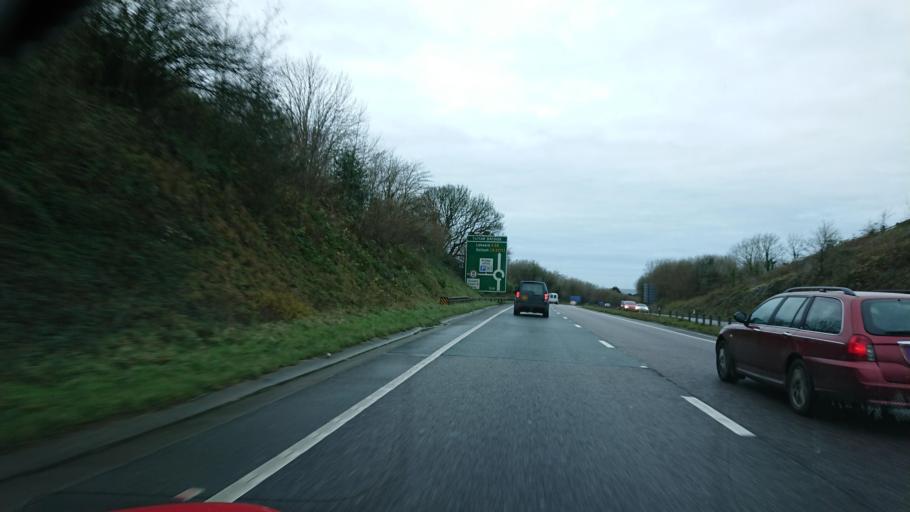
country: GB
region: England
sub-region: Cornwall
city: Torpoint
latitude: 50.4097
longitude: -4.1841
